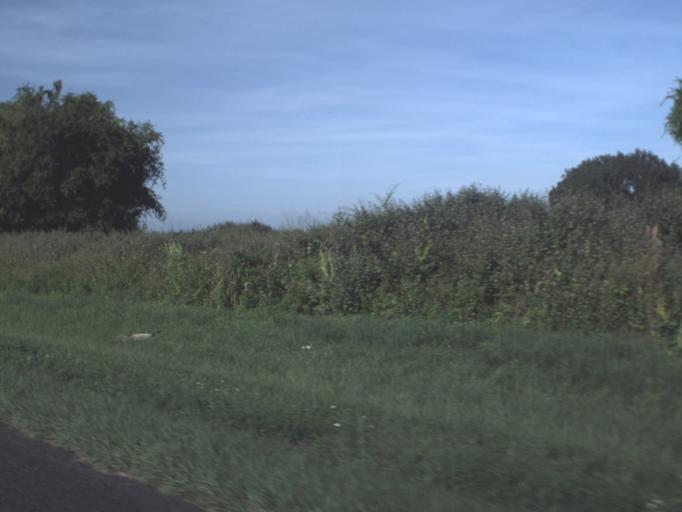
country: US
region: Florida
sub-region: DeSoto County
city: Nocatee
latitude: 27.1216
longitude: -81.9147
